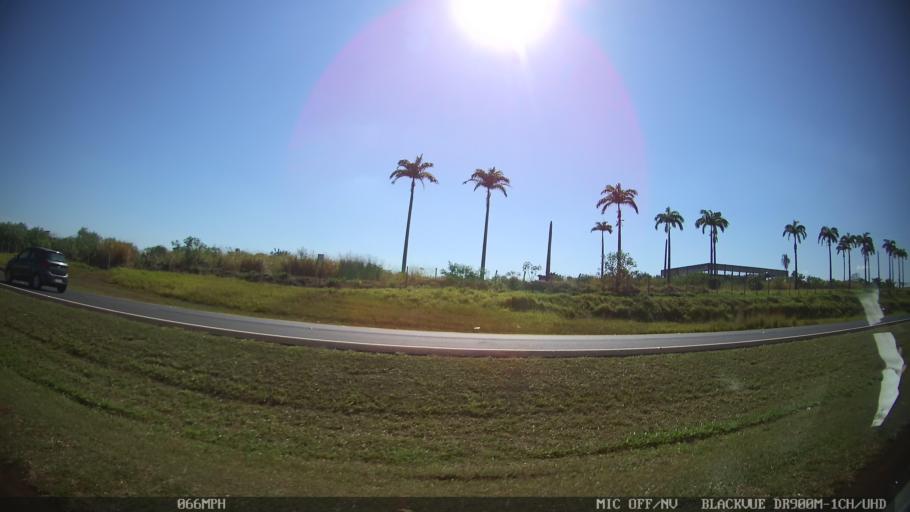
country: BR
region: Sao Paulo
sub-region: Ribeirao Preto
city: Ribeirao Preto
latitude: -21.1144
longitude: -47.8232
